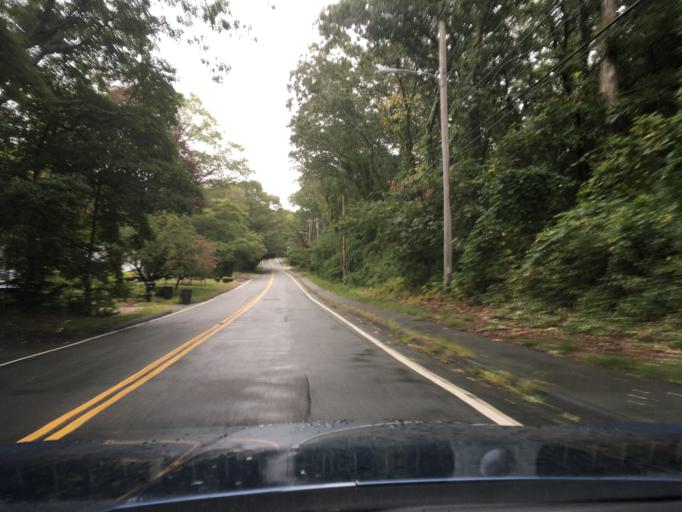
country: US
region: Rhode Island
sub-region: Kent County
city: East Greenwich
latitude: 41.6464
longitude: -71.4833
